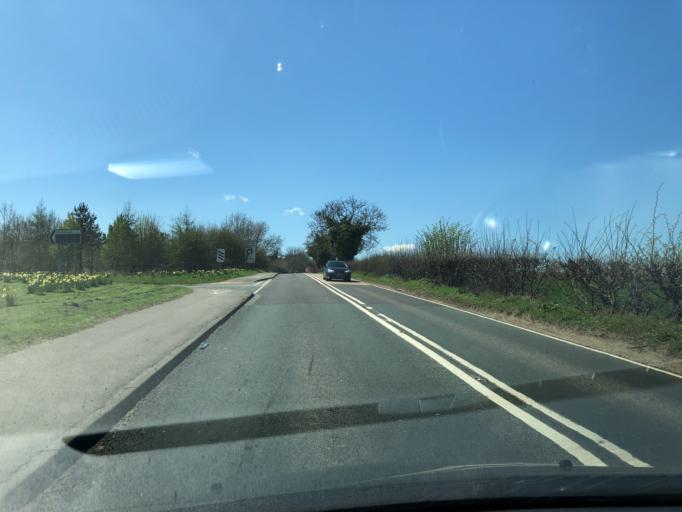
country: GB
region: England
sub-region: North Yorkshire
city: Catterick
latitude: 54.3810
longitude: -1.6718
